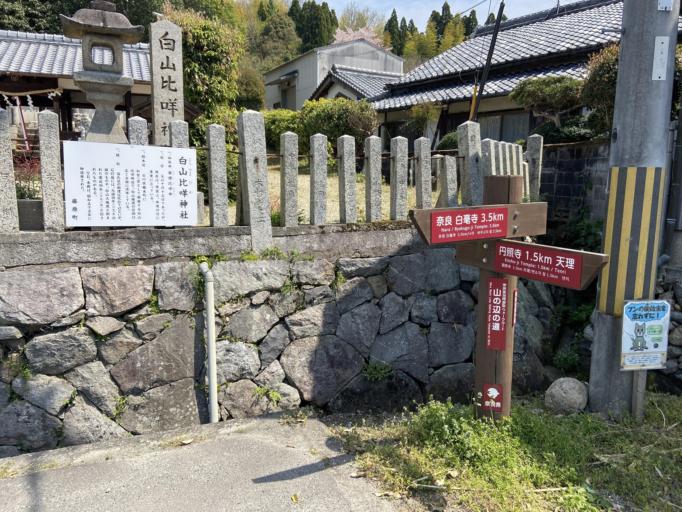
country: JP
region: Nara
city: Nara-shi
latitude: 34.6496
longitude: 135.8465
